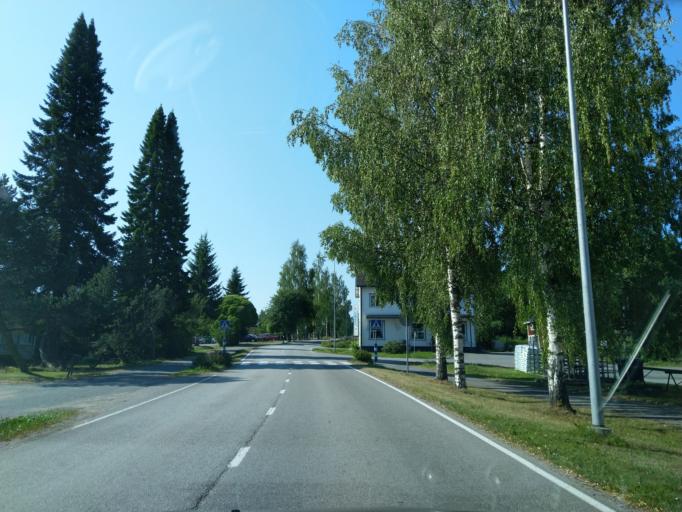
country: FI
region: Satakunta
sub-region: Pori
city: Pomarkku
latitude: 61.6925
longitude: 22.0069
